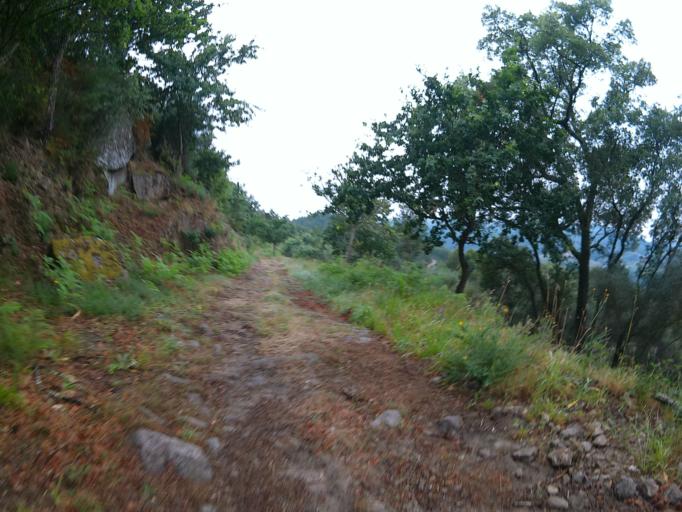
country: PT
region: Viana do Castelo
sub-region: Ponte de Lima
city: Ponte de Lima
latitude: 41.7222
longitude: -8.6091
